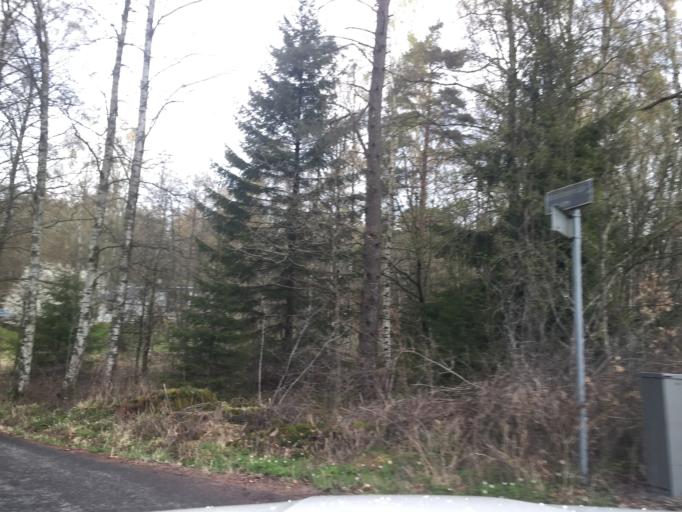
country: SE
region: Vaestra Goetaland
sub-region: Ale Kommun
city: Surte
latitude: 57.8447
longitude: 11.9940
